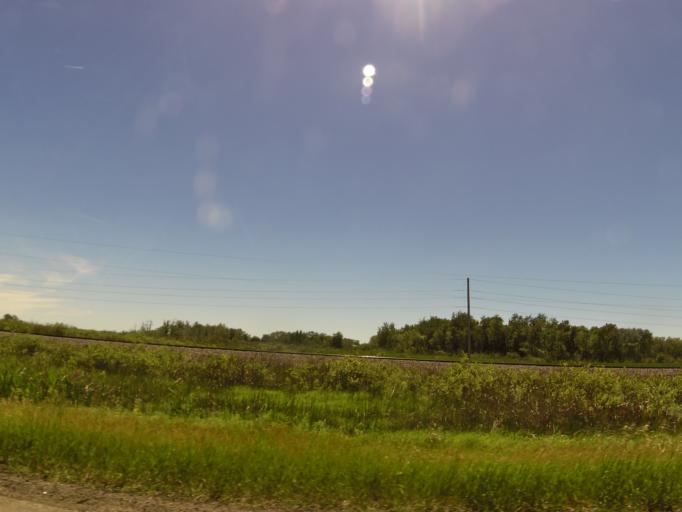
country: US
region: Minnesota
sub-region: Wadena County
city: Wadena
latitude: 46.4238
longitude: -95.0852
